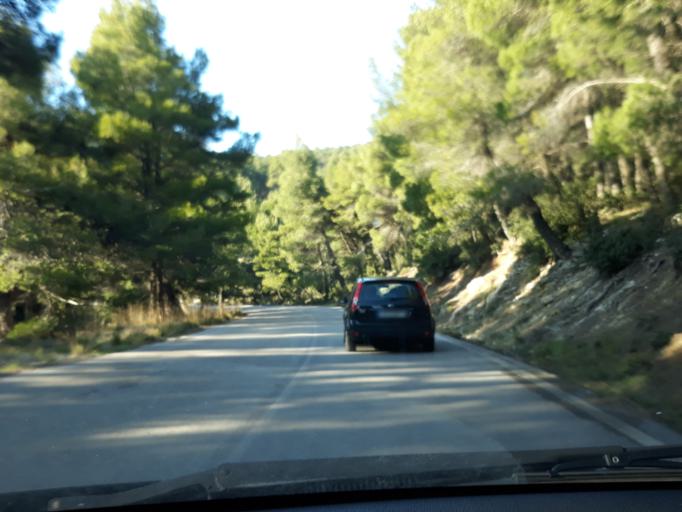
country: GR
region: Attica
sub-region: Nomarchia Dytikis Attikis
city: Fyli
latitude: 38.1456
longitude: 23.6389
